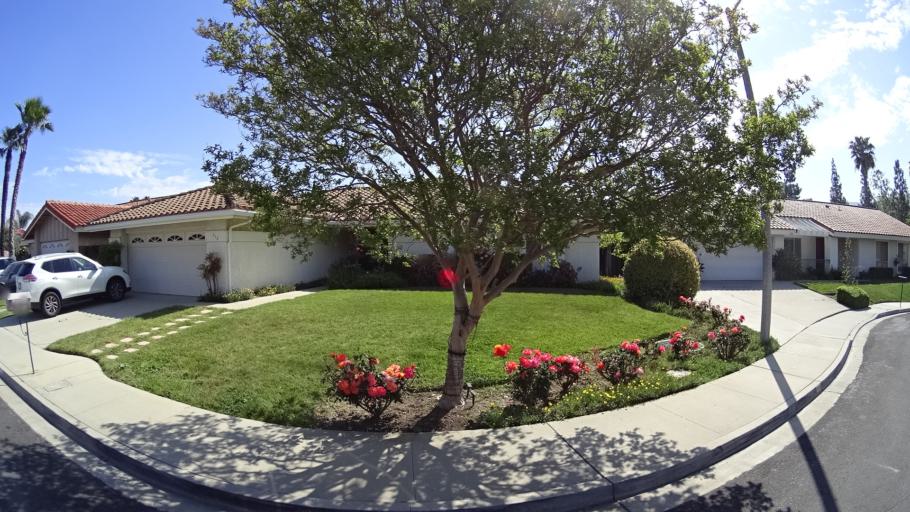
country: US
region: California
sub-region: Ventura County
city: Casa Conejo
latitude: 34.1818
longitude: -118.9306
